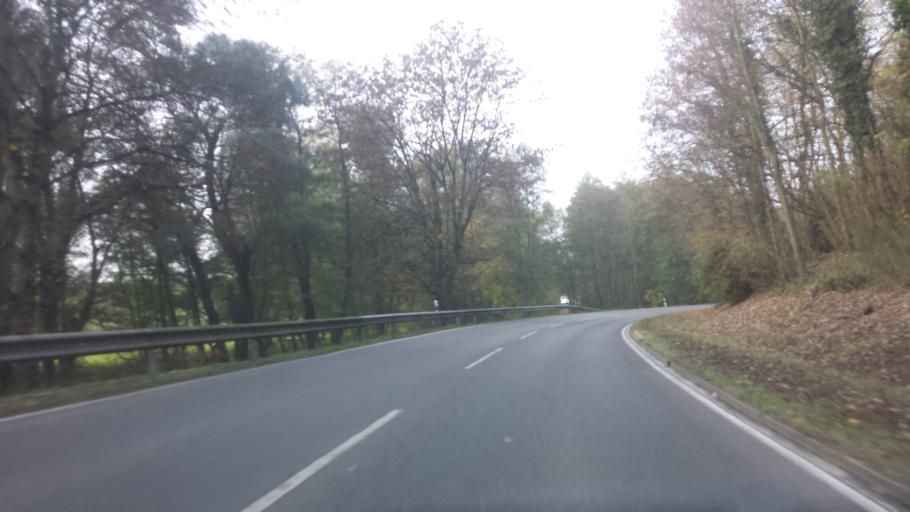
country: DE
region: Baden-Wuerttemberg
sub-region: Karlsruhe Region
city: Dielheim
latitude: 49.2934
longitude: 8.7230
